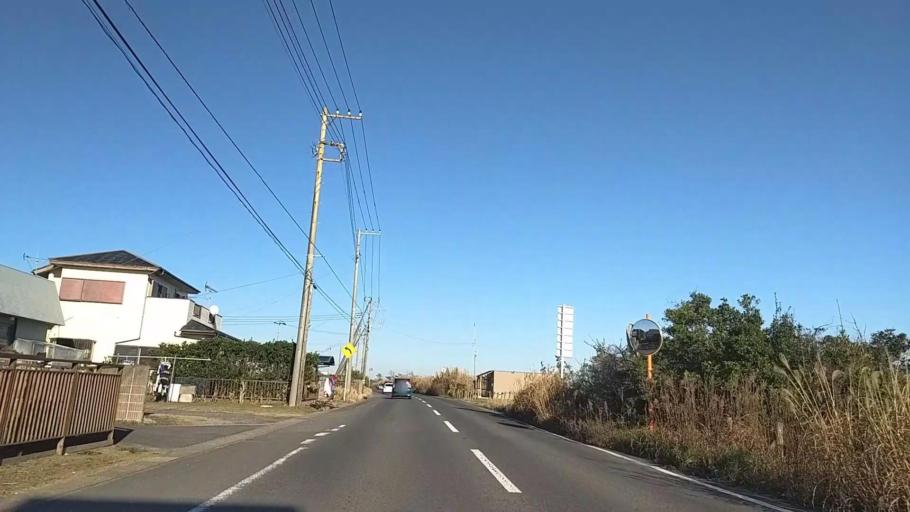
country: JP
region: Chiba
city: Asahi
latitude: 35.6711
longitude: 140.6175
